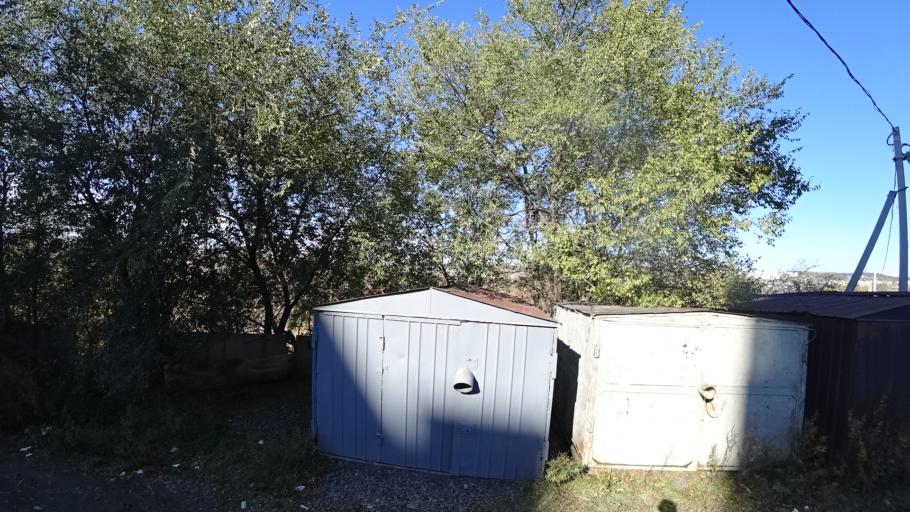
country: RU
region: Khabarovsk Krai
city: Amursk
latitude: 50.2194
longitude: 136.8942
